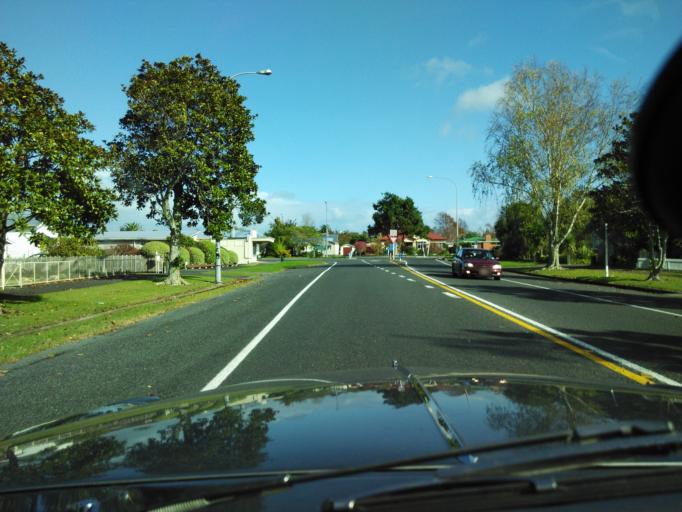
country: NZ
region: Waikato
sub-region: Hauraki District
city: Paeroa
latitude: -37.5496
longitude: 175.7030
